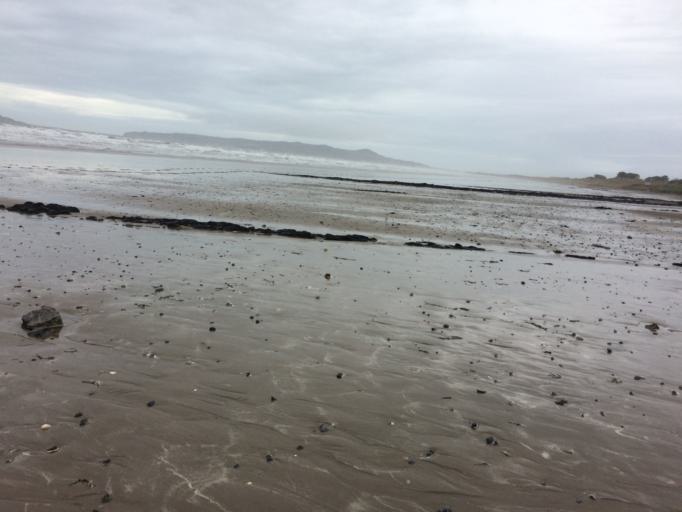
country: IE
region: Leinster
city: Portmarnock
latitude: 53.4322
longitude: -6.1238
